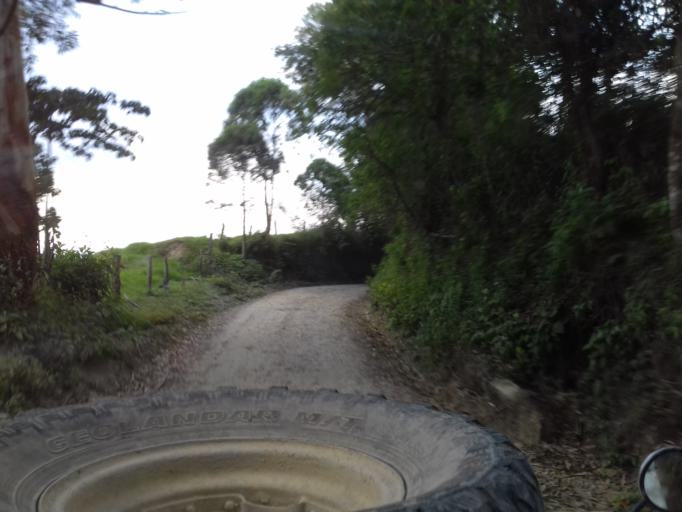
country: CO
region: Quindio
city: Salento
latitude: 4.6187
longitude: -75.5558
